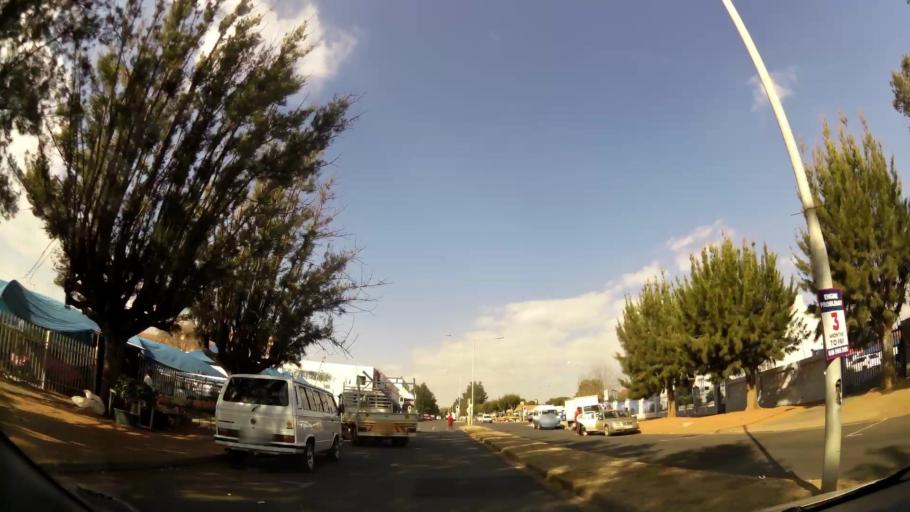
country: ZA
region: Gauteng
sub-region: West Rand District Municipality
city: Krugersdorp
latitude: -26.1042
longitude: 27.7695
